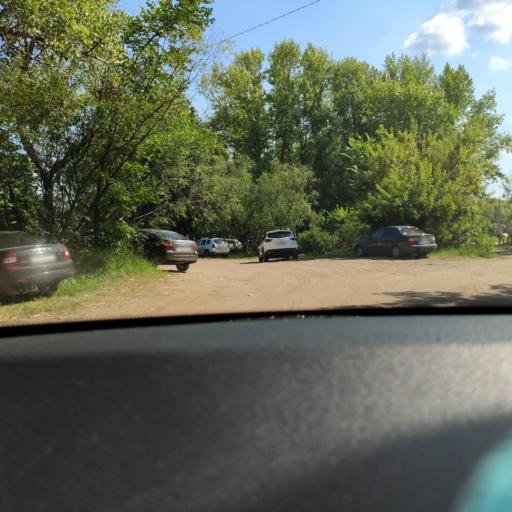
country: RU
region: Samara
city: Volzhskiy
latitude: 53.4327
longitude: 50.1664
